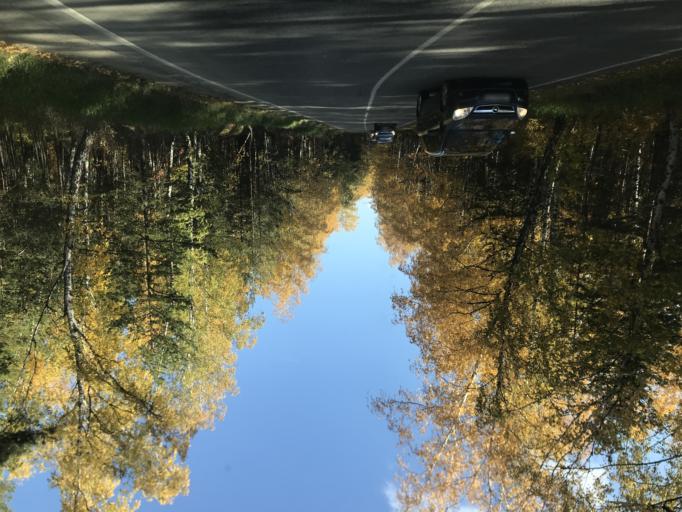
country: RU
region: Chelyabinsk
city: Dolgoderevenskoye
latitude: 55.2824
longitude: 61.3630
